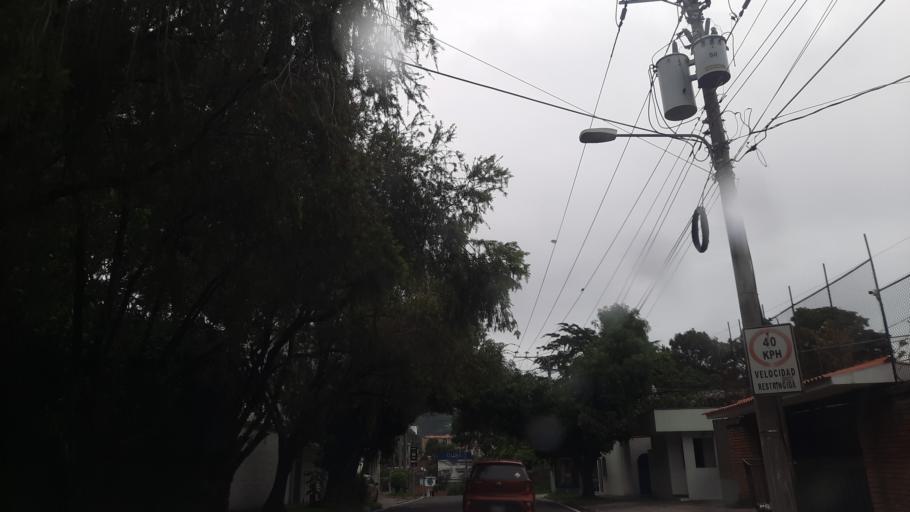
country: SV
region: La Libertad
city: Antiguo Cuscatlan
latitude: 13.6959
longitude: -89.2446
